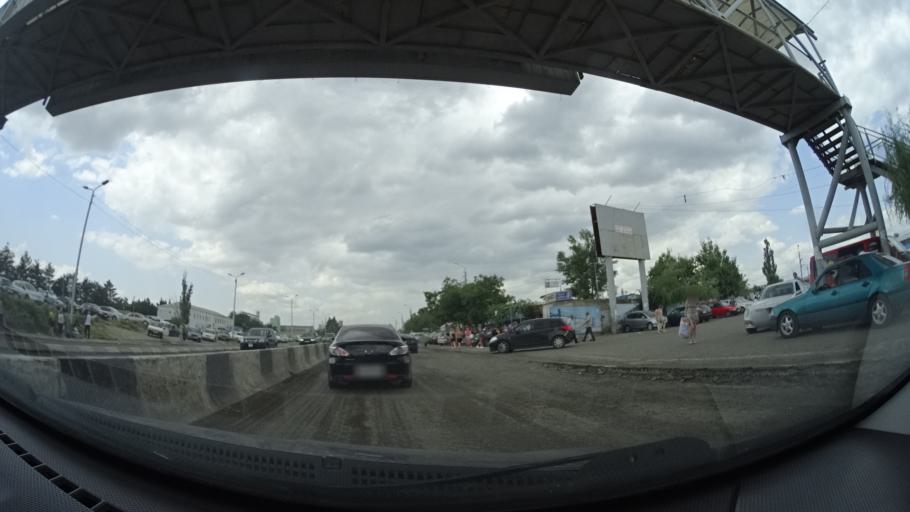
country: GE
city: Didi Lilo
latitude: 41.6915
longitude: 45.0006
